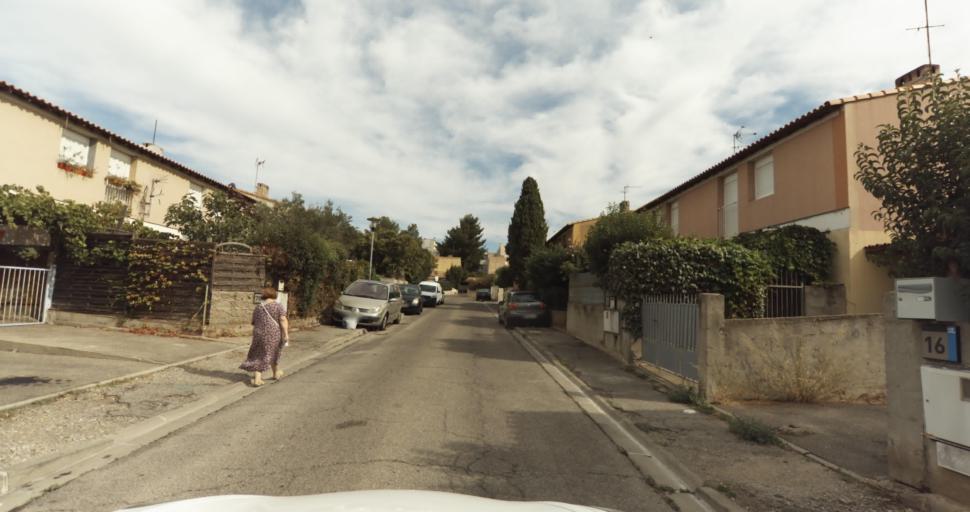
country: FR
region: Provence-Alpes-Cote d'Azur
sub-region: Departement des Bouches-du-Rhone
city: Miramas
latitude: 43.5935
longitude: 5.0071
